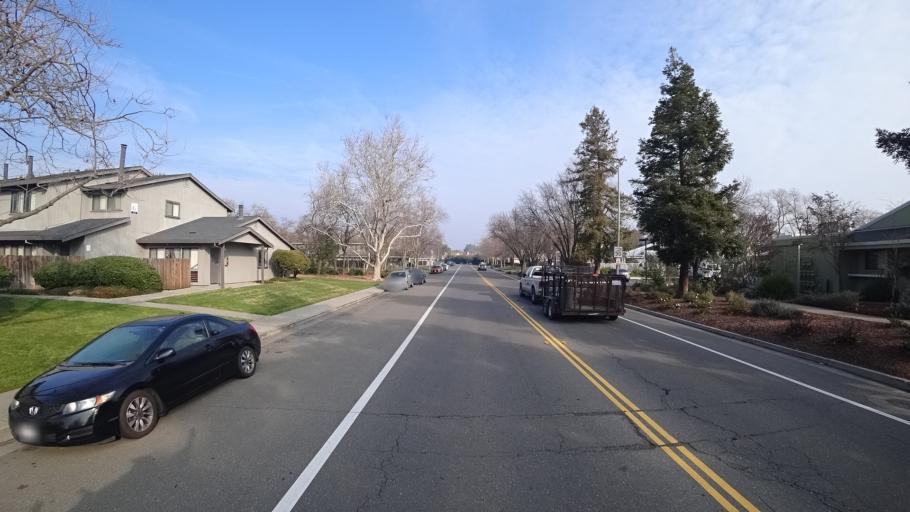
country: US
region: California
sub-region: Yolo County
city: Davis
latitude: 38.5650
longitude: -121.7658
